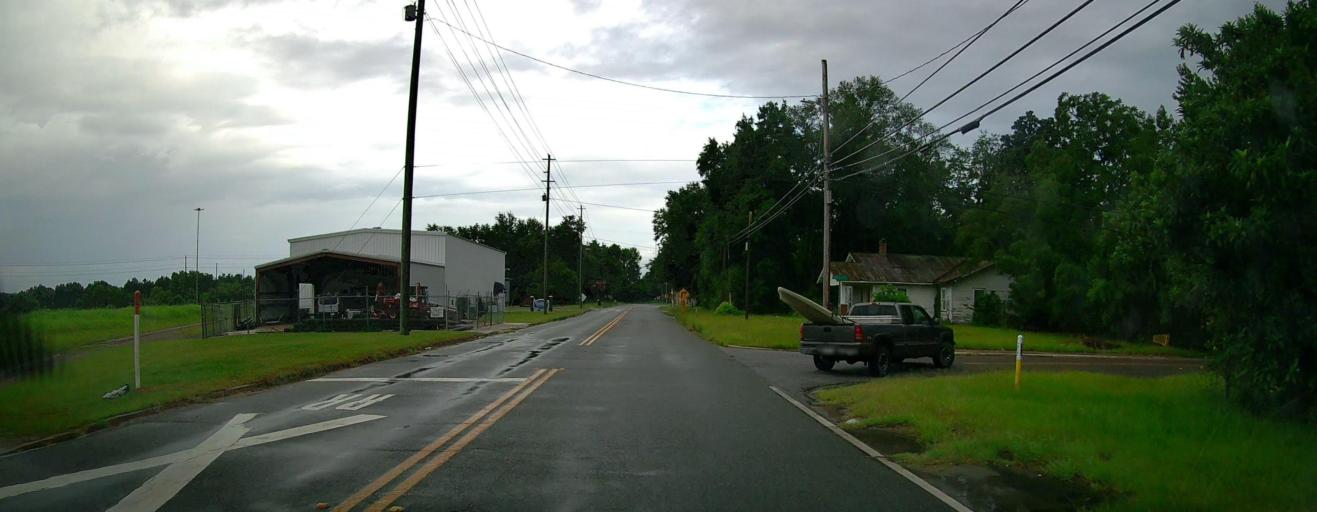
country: US
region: Georgia
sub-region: Ware County
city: Waycross
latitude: 31.2069
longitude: -82.3659
